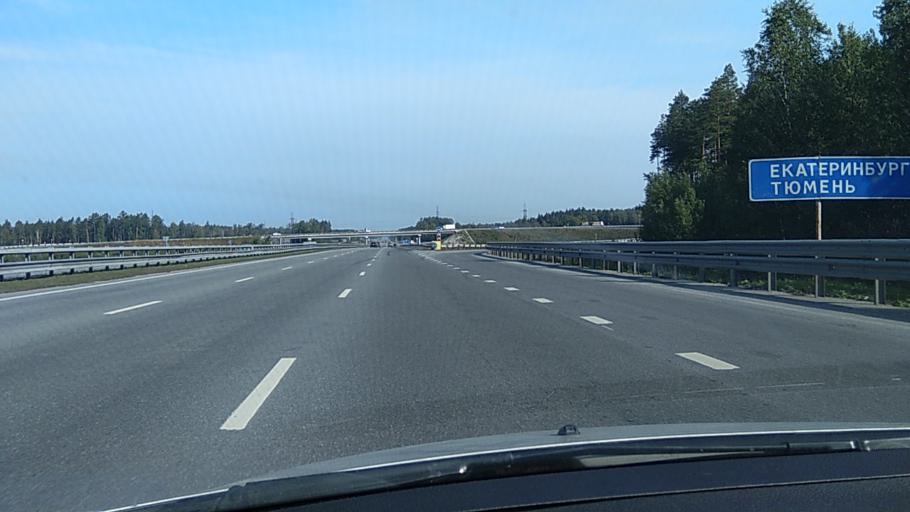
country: RU
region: Sverdlovsk
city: Shuvakish
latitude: 56.9314
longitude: 60.5106
